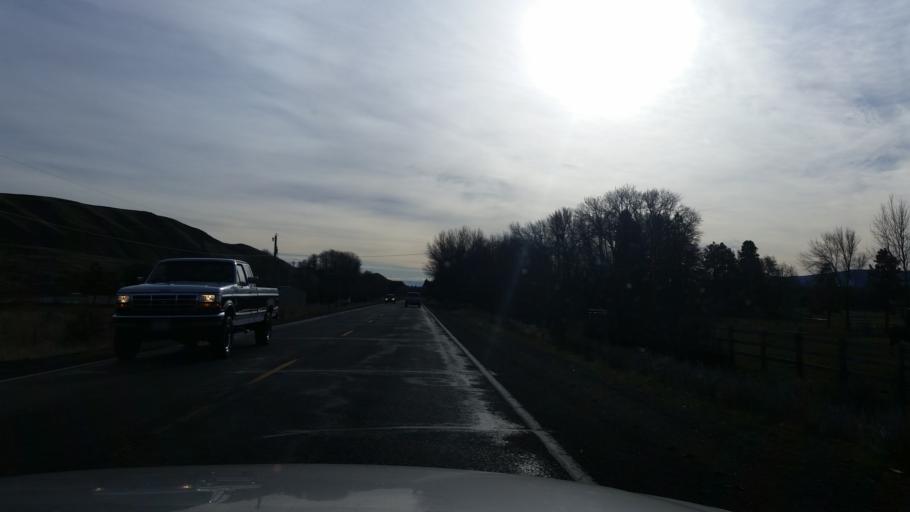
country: US
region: Washington
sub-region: Kittitas County
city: Ellensburg
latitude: 47.0912
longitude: -120.6833
